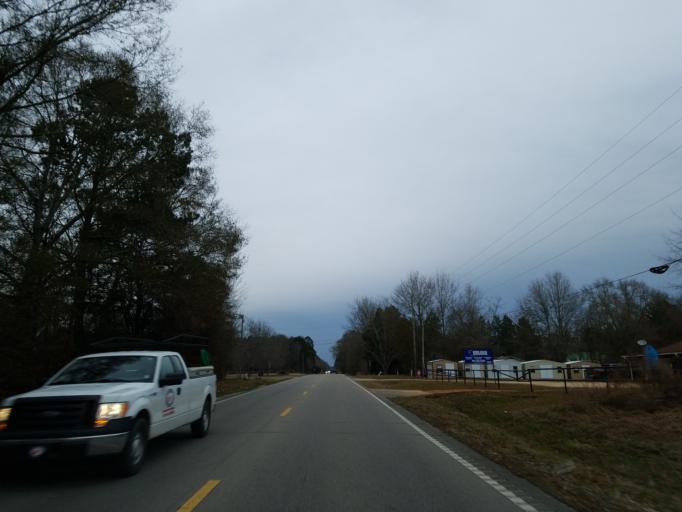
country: US
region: Mississippi
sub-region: Forrest County
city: Glendale
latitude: 31.4900
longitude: -89.2810
